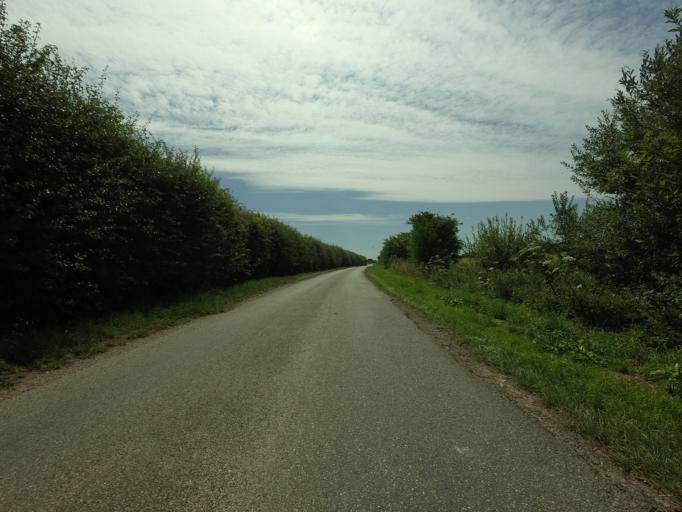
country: GB
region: England
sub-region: Kent
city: Stone
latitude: 51.0134
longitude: 0.7953
